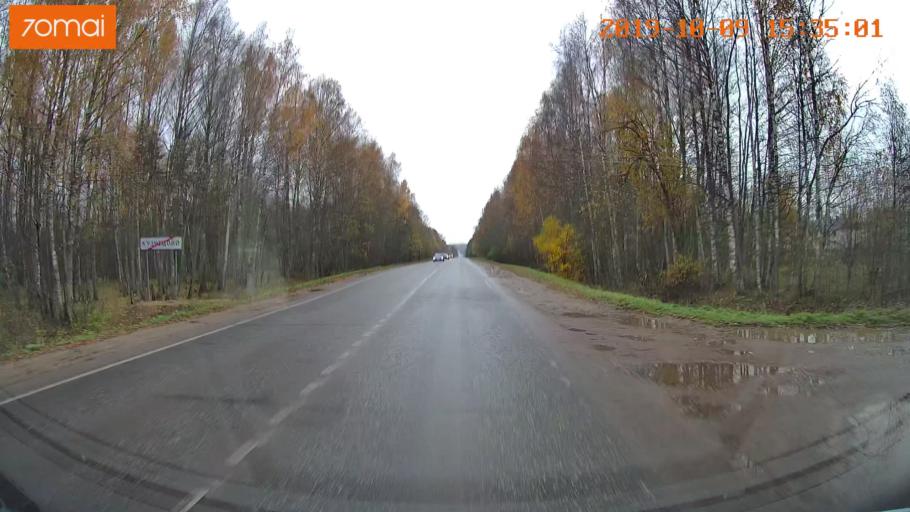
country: RU
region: Kostroma
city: Oktyabr'skiy
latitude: 57.9362
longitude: 41.2355
